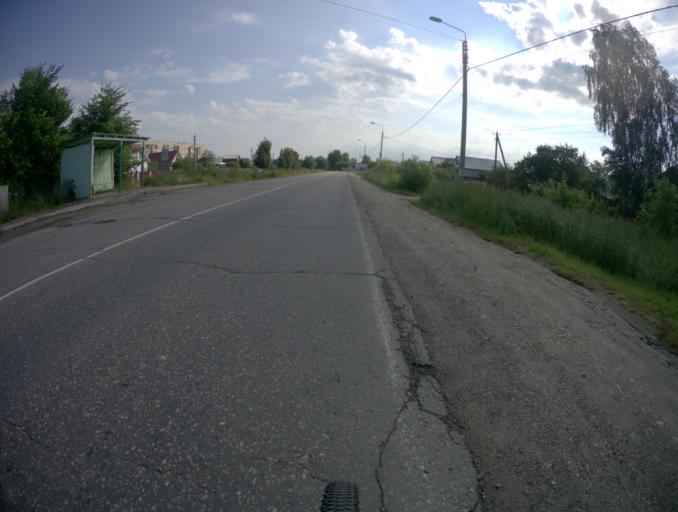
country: RU
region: Vladimir
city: Novovyazniki
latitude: 56.2116
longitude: 42.1718
